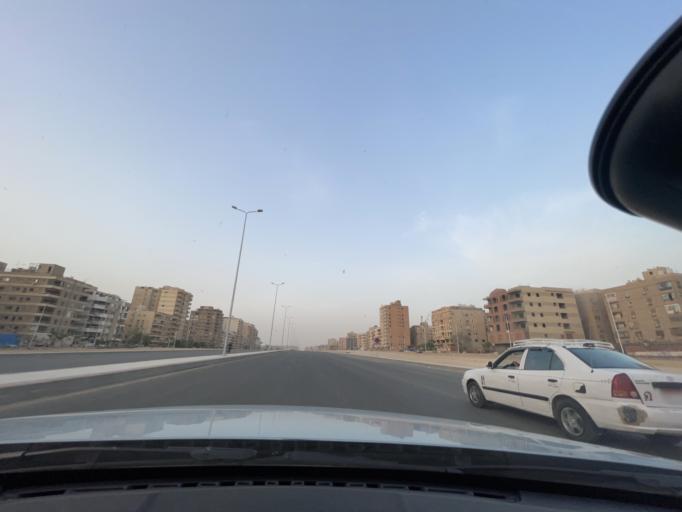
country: EG
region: Muhafazat al Qahirah
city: Cairo
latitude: 30.0507
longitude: 31.3688
